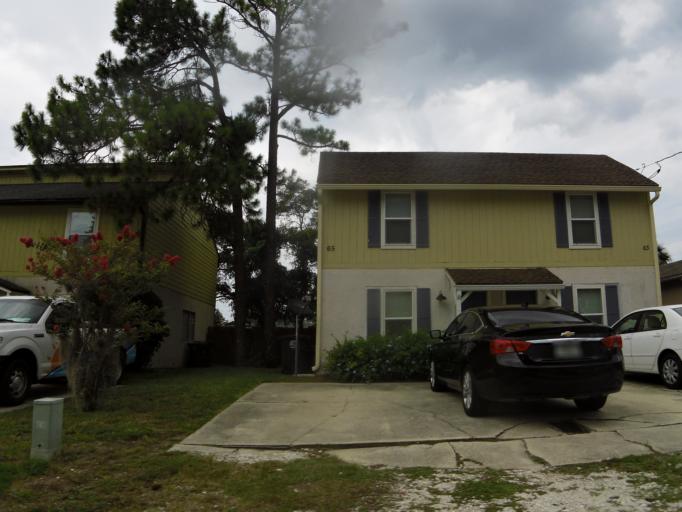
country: US
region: Florida
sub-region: Duval County
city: Atlantic Beach
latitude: 30.3303
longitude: -81.4185
